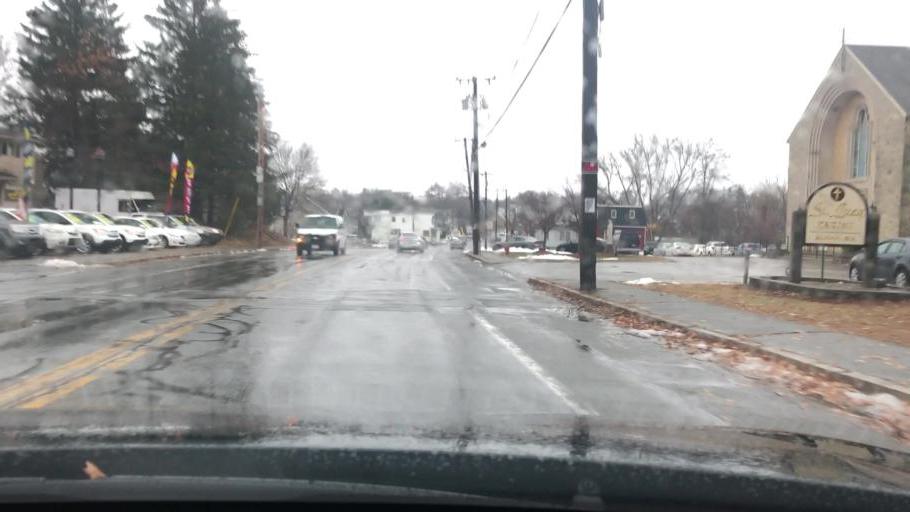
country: US
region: Massachusetts
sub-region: Essex County
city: North Andover
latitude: 42.7380
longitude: -71.1326
